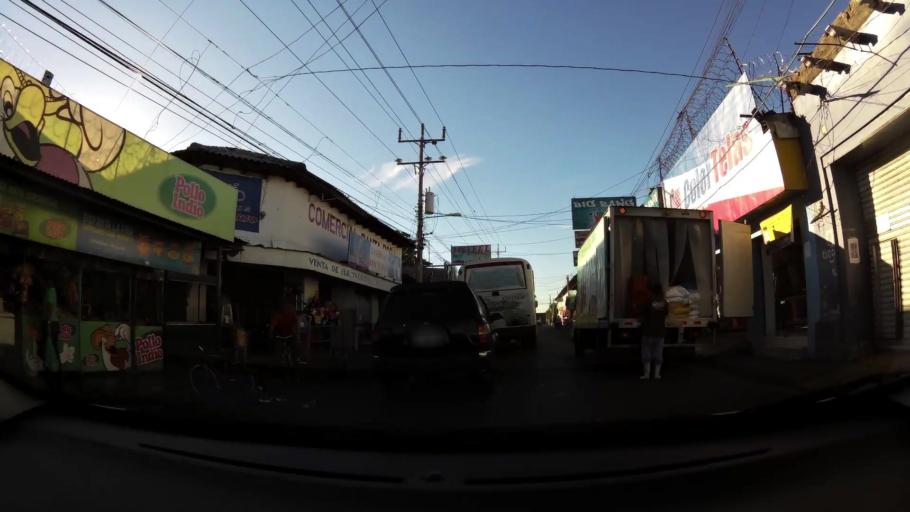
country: SV
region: San Miguel
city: San Miguel
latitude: 13.4842
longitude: -88.1723
